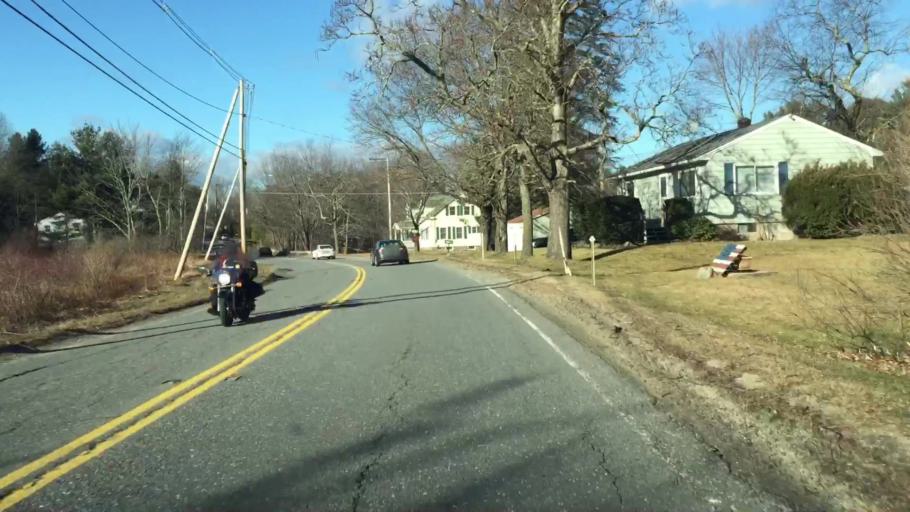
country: US
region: Massachusetts
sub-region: Worcester County
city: Sterling
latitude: 42.4149
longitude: -71.8019
